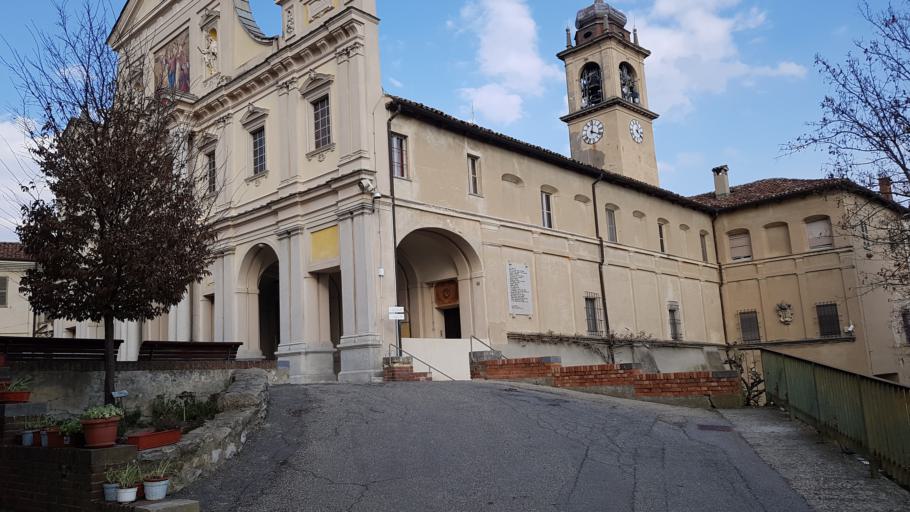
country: IT
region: Piedmont
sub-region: Provincia di Alessandria
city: Serralunga di Crea
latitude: 45.0940
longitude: 8.2755
